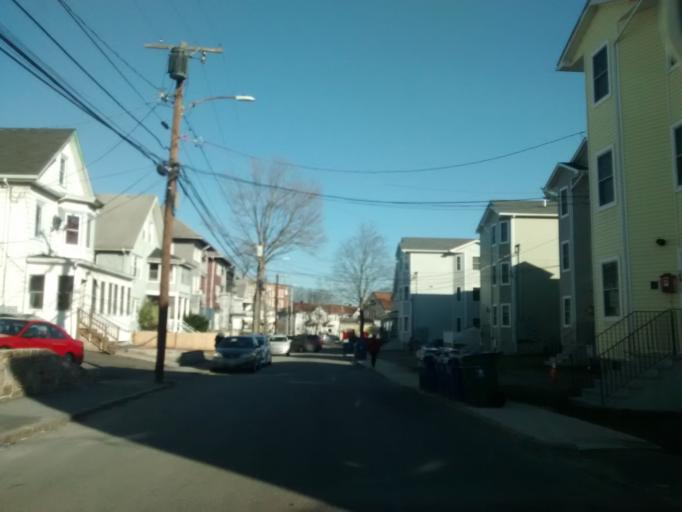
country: US
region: Massachusetts
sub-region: Middlesex County
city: Framingham
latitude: 42.2794
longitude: -71.4149
